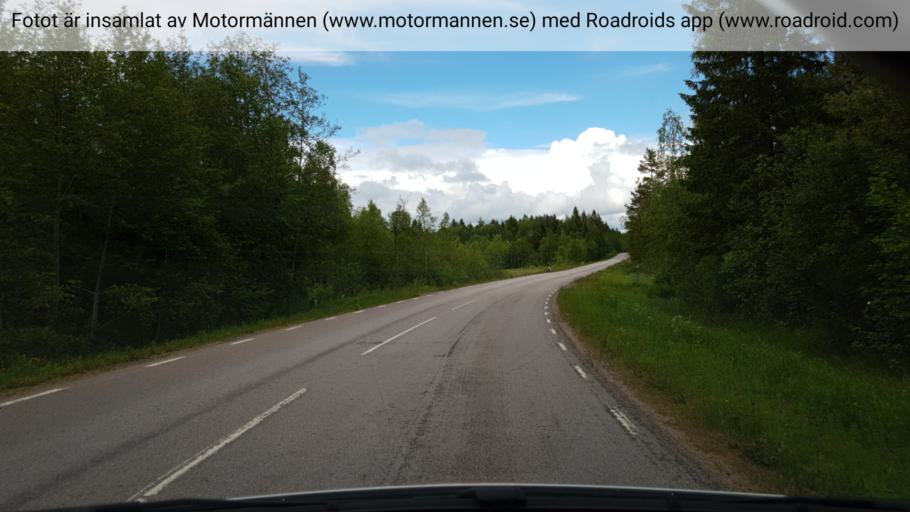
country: SE
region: Vaesterbotten
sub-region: Umea Kommun
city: Hoernefors
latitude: 63.5764
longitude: 19.8302
